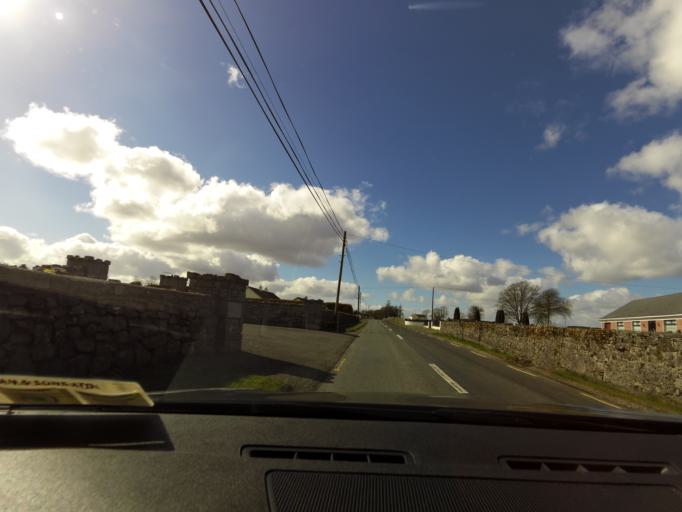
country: IE
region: Connaught
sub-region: County Galway
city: Loughrea
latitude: 53.4221
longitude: -8.5488
